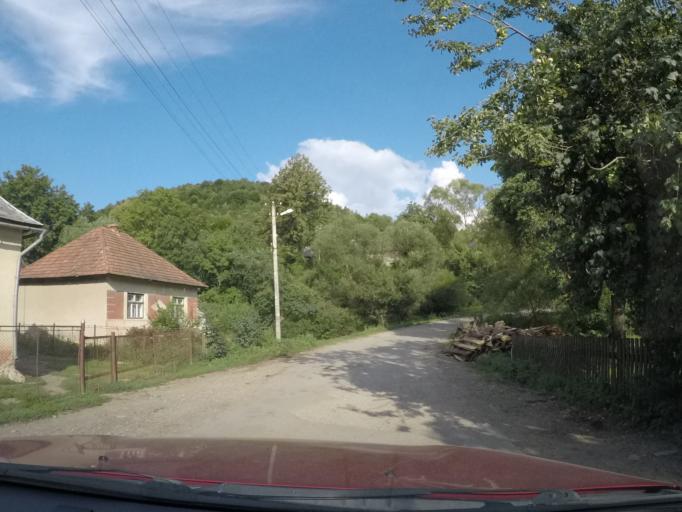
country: UA
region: Zakarpattia
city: Velykyi Bereznyi
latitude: 49.0079
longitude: 22.6385
